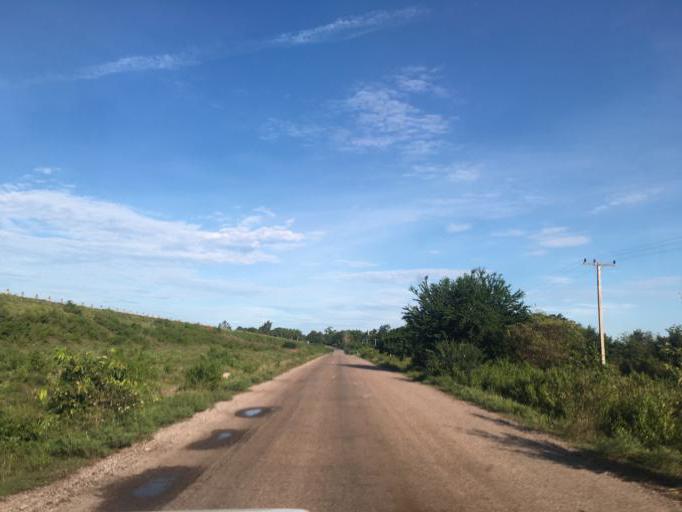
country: TH
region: Changwat Udon Thani
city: Kut Chap
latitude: 17.3603
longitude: 102.5703
